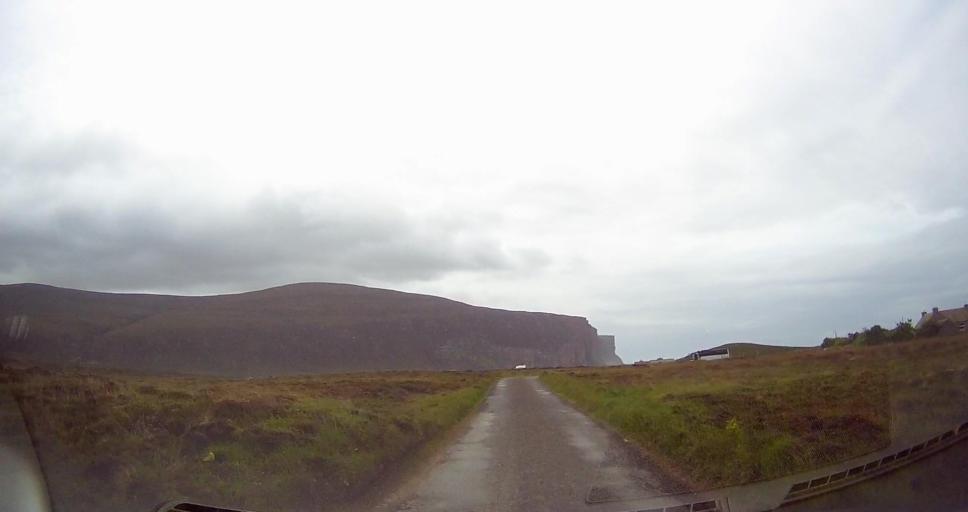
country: GB
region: Scotland
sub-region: Orkney Islands
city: Stromness
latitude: 58.8746
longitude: -3.3864
